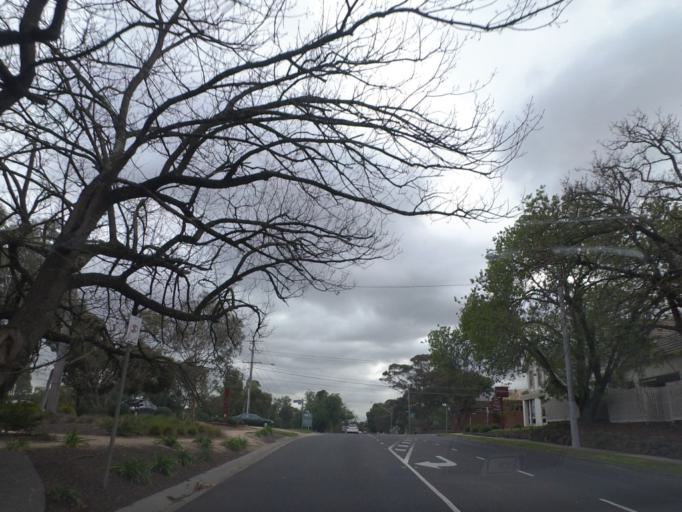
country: AU
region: Victoria
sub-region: Nillumbik
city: Eltham
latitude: -37.7214
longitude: 145.1458
